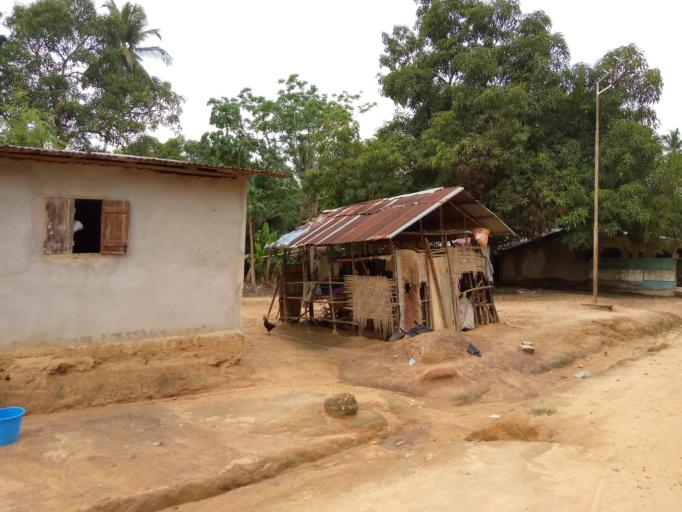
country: SL
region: Western Area
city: Waterloo
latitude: 8.3349
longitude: -12.9415
